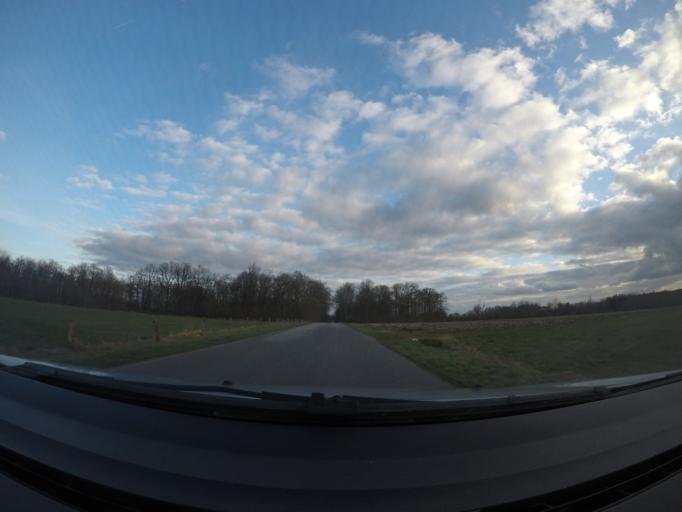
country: BE
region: Wallonia
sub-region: Province du Luxembourg
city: Etalle
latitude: 49.6904
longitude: 5.5620
